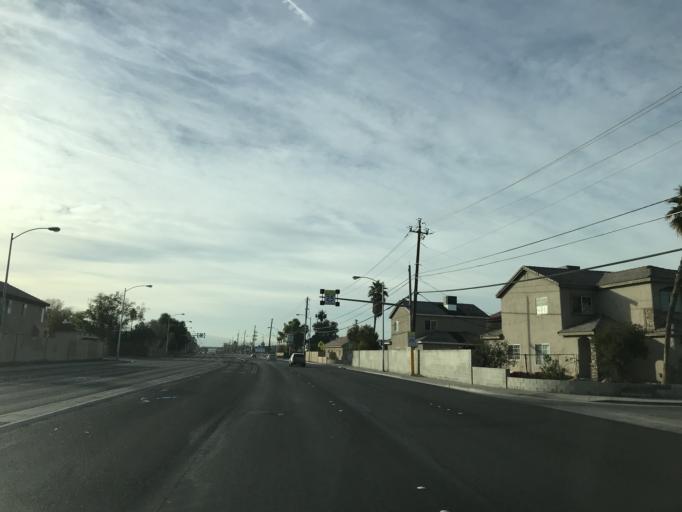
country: US
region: Nevada
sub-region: Clark County
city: Winchester
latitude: 36.1507
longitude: -115.0654
